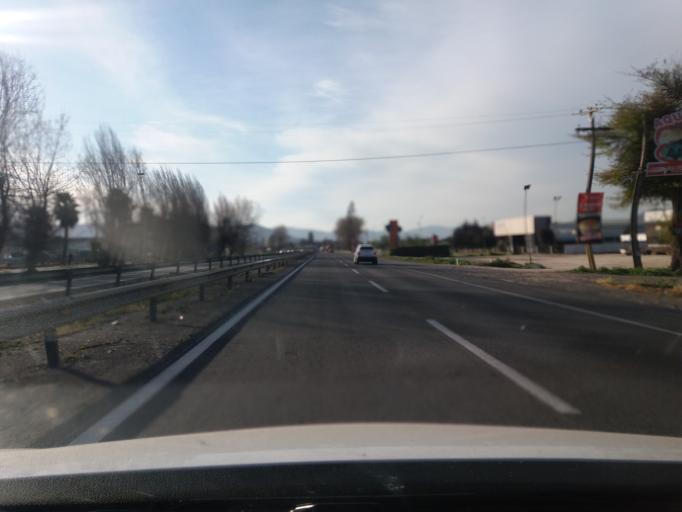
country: CL
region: Valparaiso
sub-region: Provincia de Quillota
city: Hacienda La Calera
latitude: -32.7962
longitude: -71.1598
